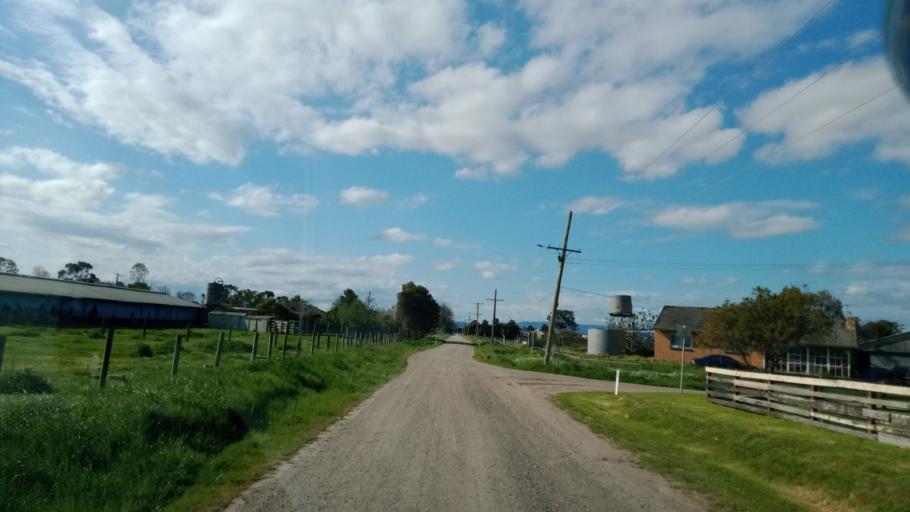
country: AU
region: Victoria
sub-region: Casey
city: Cranbourne West
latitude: -38.0846
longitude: 145.2500
